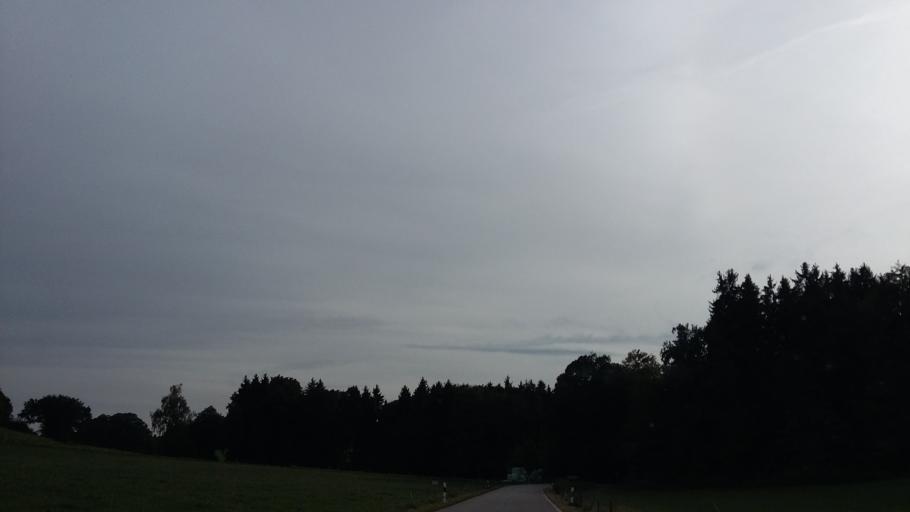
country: DE
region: Bavaria
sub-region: Upper Bavaria
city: Munsing
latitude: 47.8773
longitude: 11.3415
